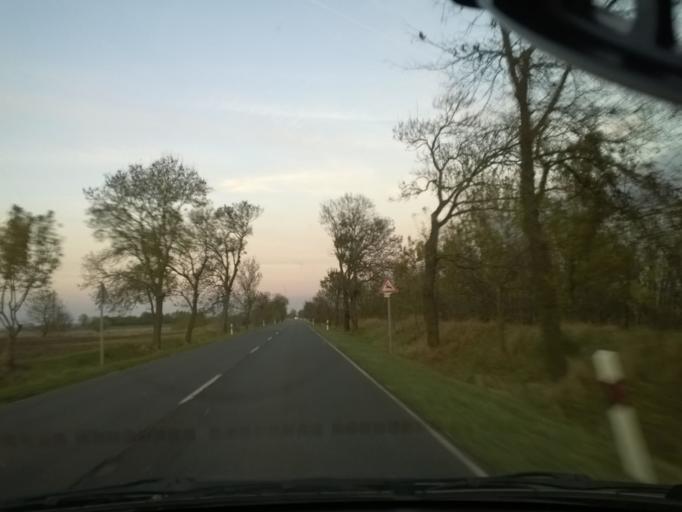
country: HU
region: Csongrad
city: Tomorkeny
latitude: 46.6996
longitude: 20.0302
